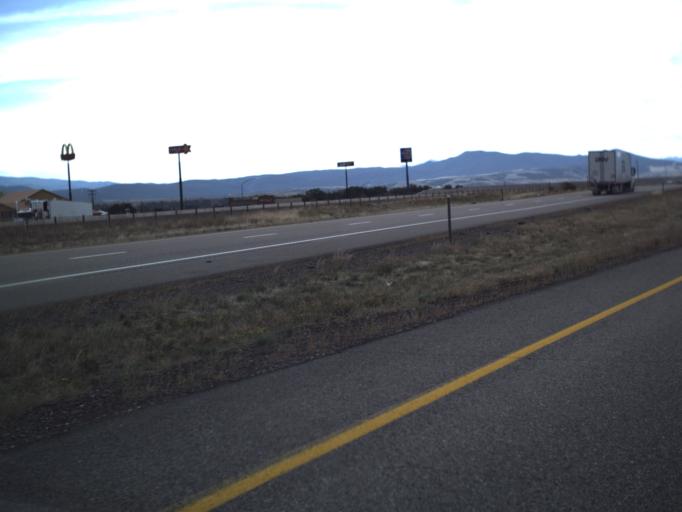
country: US
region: Utah
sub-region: Beaver County
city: Beaver
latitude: 38.2965
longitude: -112.6517
